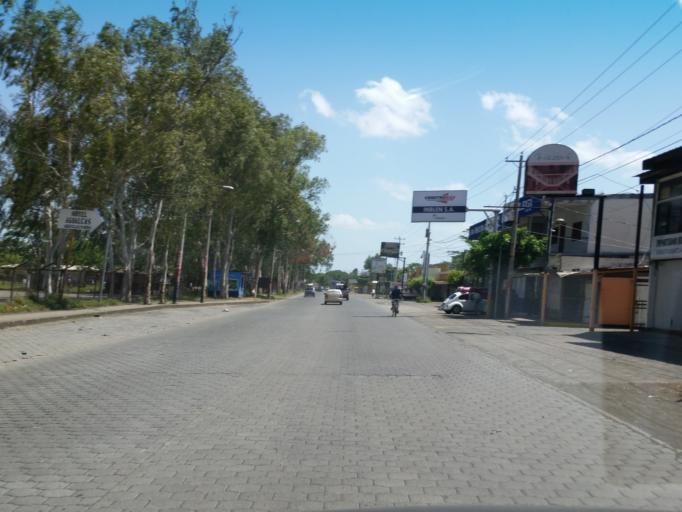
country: NI
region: Managua
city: Managua
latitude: 12.1445
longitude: -86.1952
